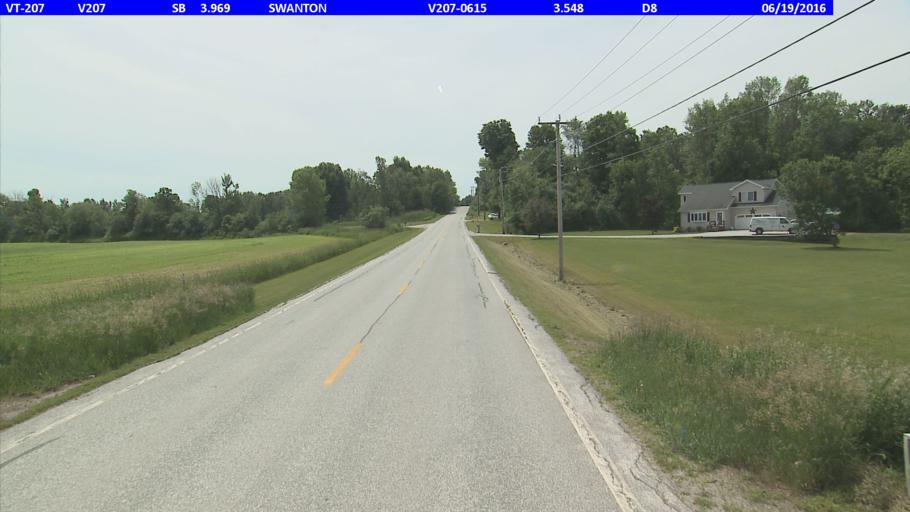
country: US
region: Vermont
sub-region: Franklin County
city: Swanton
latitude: 44.8951
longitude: -73.0672
